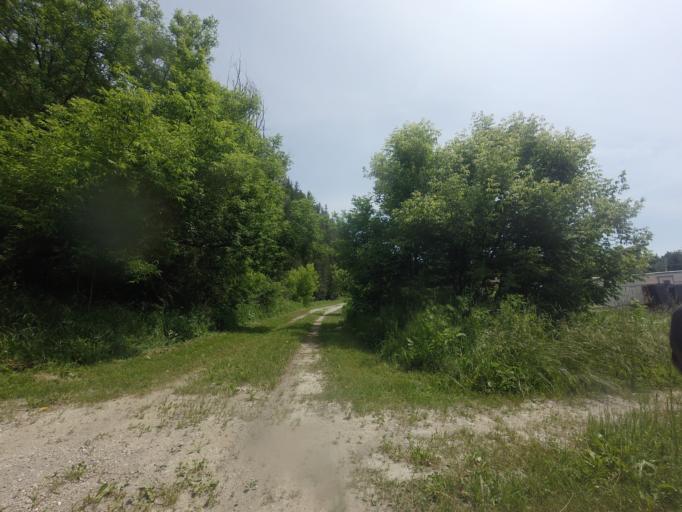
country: CA
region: Quebec
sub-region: Outaouais
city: Wakefield
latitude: 45.8483
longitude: -75.9868
